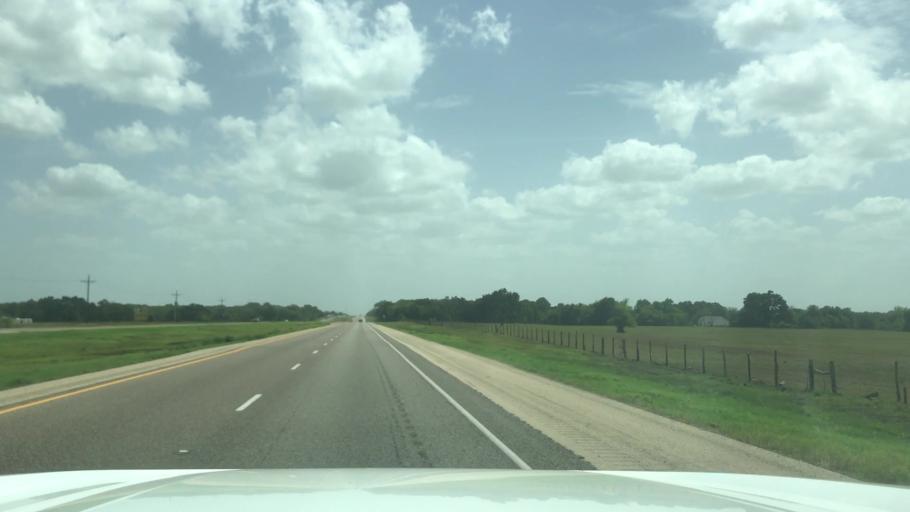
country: US
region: Texas
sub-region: Robertson County
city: Calvert
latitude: 31.0732
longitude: -96.7131
